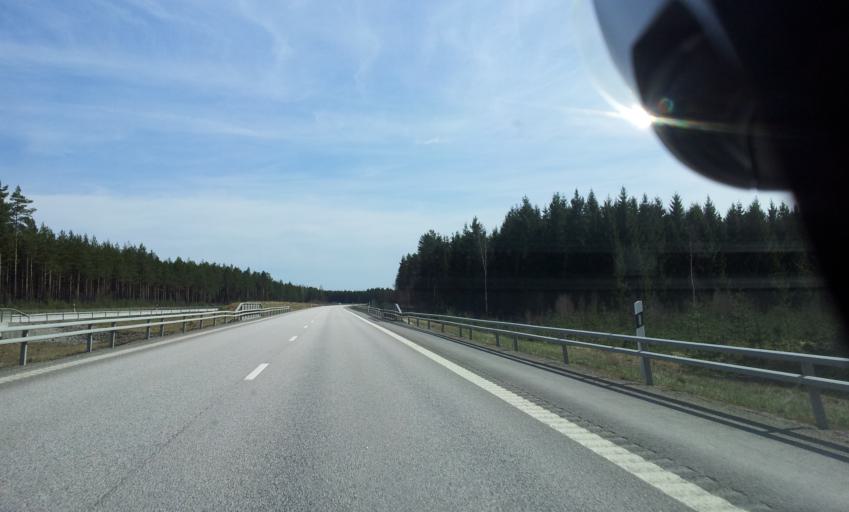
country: SE
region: Uppsala
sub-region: Osthammars Kommun
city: Bjorklinge
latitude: 60.0868
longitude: 17.5879
